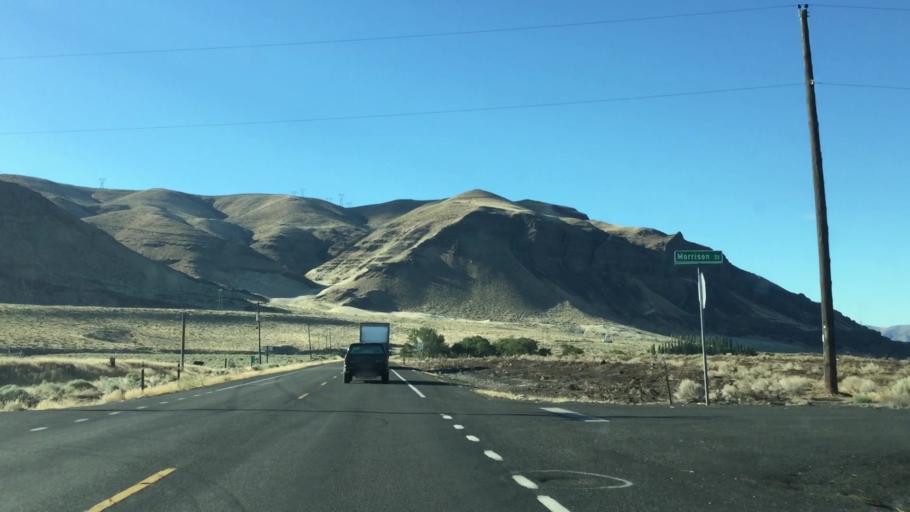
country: US
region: Washington
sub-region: Grant County
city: Mattawa
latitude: 46.8207
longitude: -119.9251
